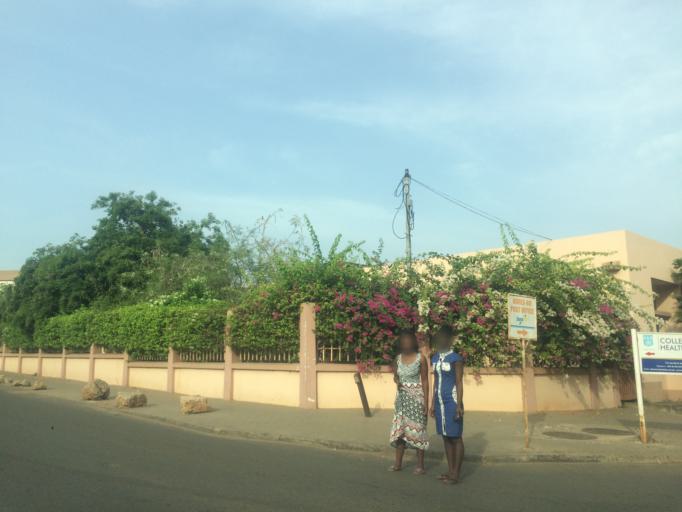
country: GH
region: Greater Accra
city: Accra
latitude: 5.5382
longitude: -0.2285
